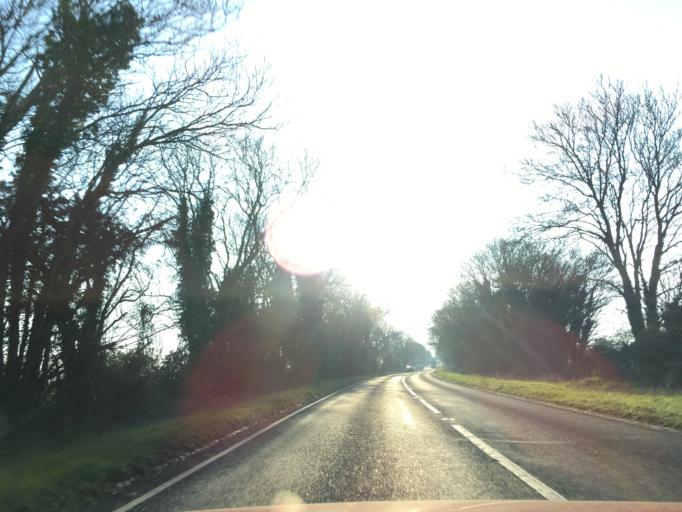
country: GB
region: England
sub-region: Gloucestershire
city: Northleach
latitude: 51.8257
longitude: -1.7950
